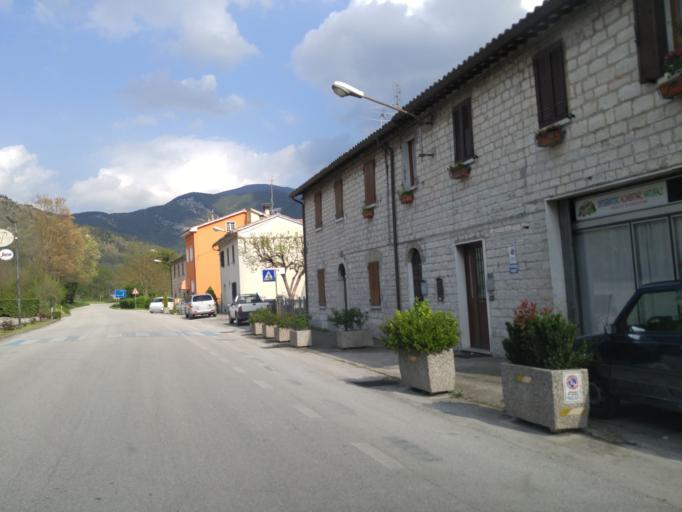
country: IT
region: The Marches
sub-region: Provincia di Pesaro e Urbino
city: Acqualagna
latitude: 43.6360
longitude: 12.6903
